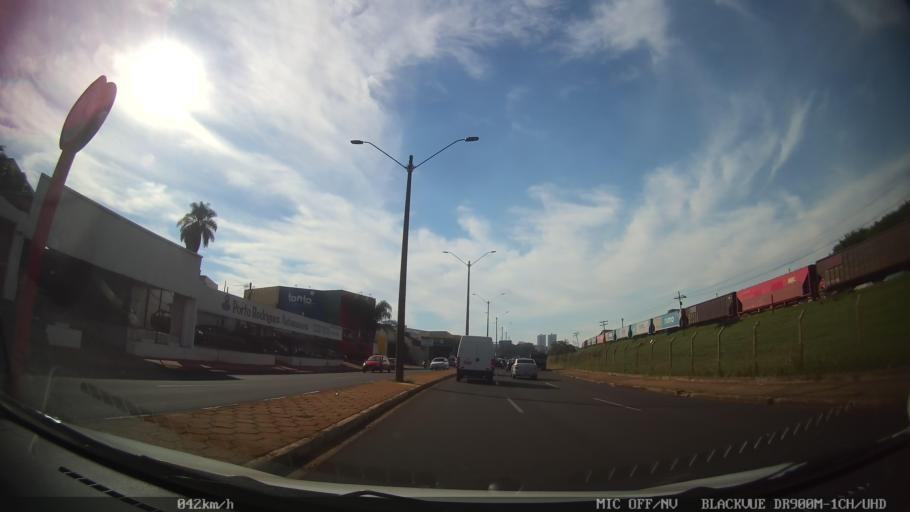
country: BR
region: Sao Paulo
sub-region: Araraquara
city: Araraquara
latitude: -21.7844
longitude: -48.1722
